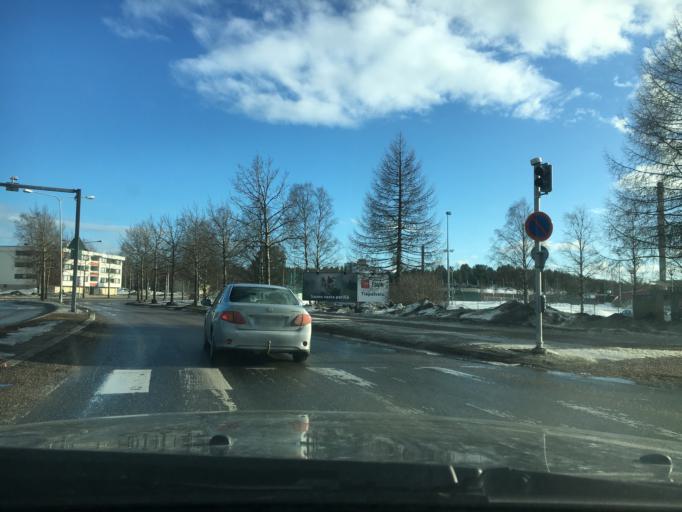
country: FI
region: Kainuu
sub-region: Kajaani
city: Kajaani
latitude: 64.2221
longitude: 27.7278
